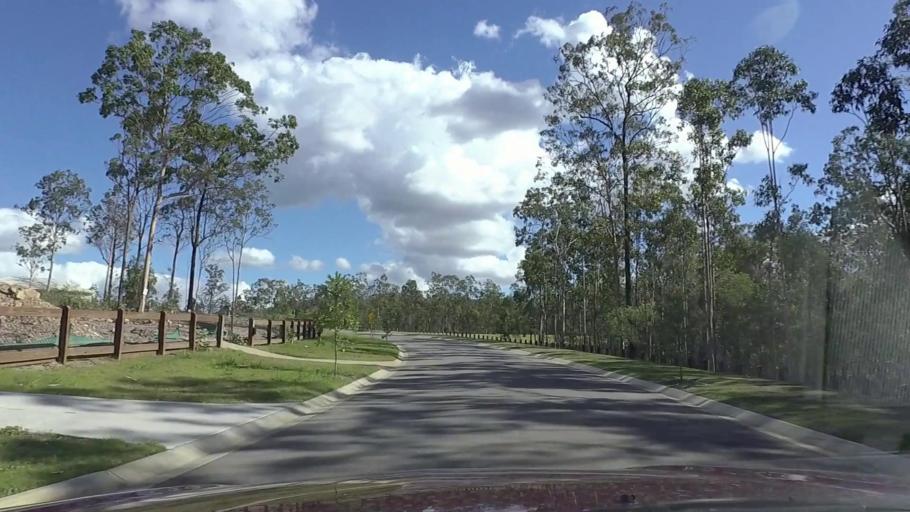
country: AU
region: Queensland
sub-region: Ipswich
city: Springfield Lakes
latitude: -27.7506
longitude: 152.9208
